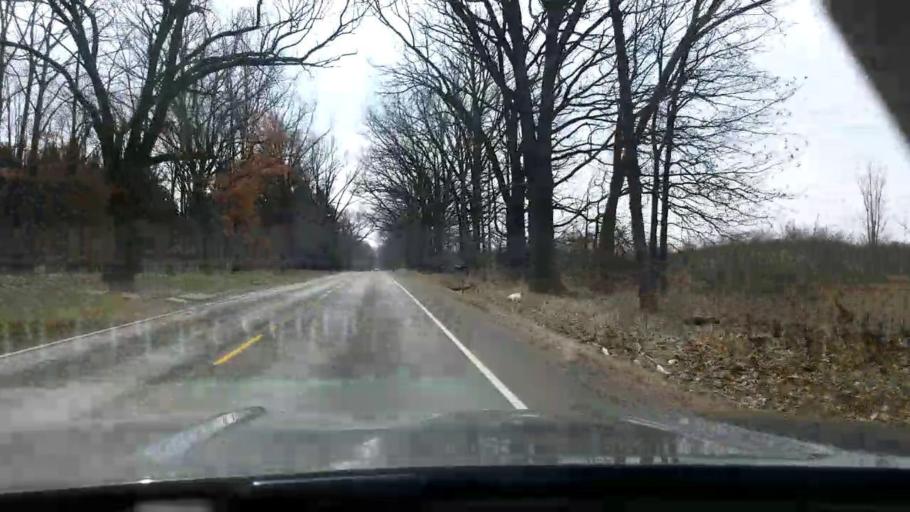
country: US
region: Michigan
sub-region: Jackson County
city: Spring Arbor
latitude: 42.1875
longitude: -84.5205
